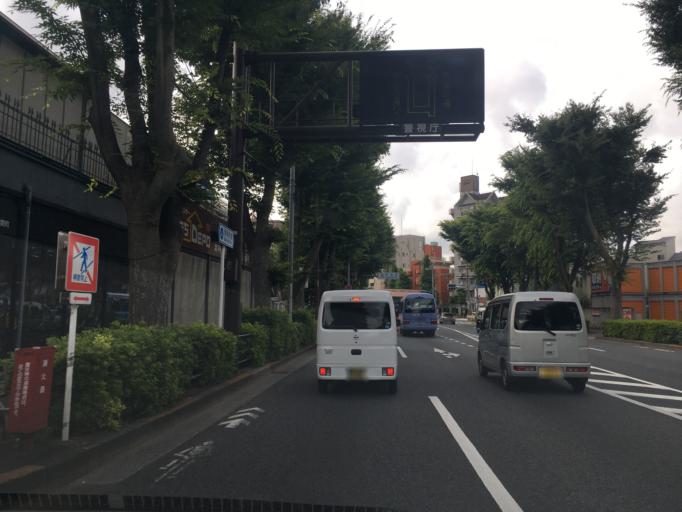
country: JP
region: Tokyo
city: Musashino
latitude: 35.7187
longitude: 139.5932
